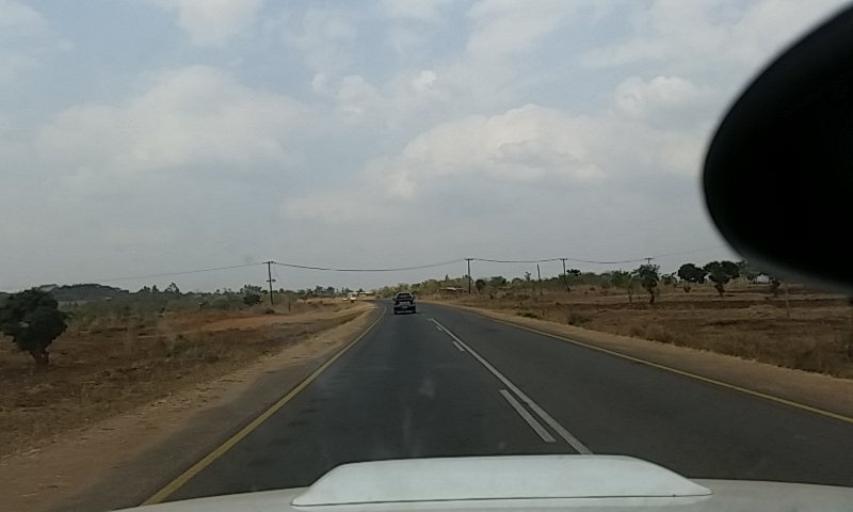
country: MW
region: Central Region
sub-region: Lilongwe District
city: Lilongwe
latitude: -13.8422
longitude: 33.8451
